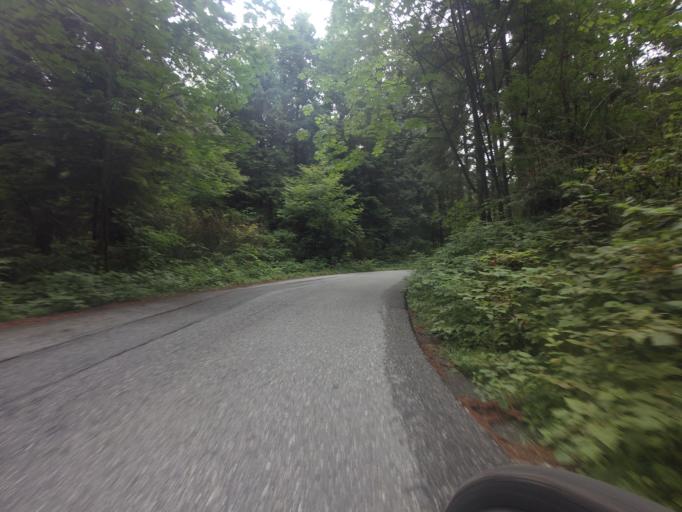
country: CA
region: British Columbia
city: West End
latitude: 49.3099
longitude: -123.1443
